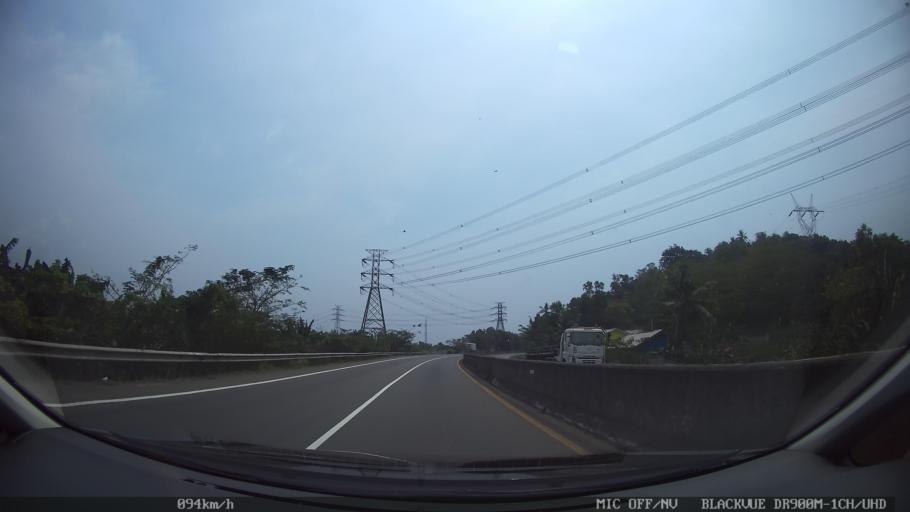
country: ID
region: Banten
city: Curug
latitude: -5.9822
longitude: 106.0268
